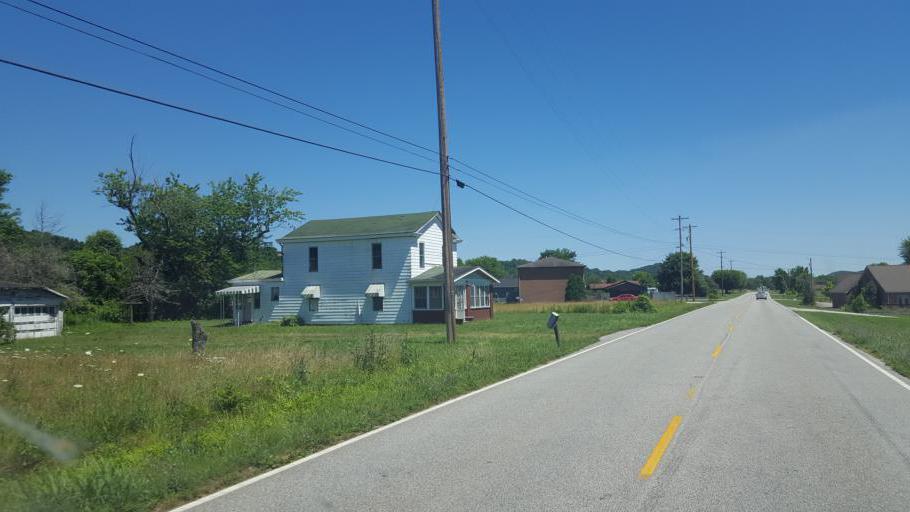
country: US
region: West Virginia
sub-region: Cabell County
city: Lesage
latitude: 38.5260
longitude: -82.3059
